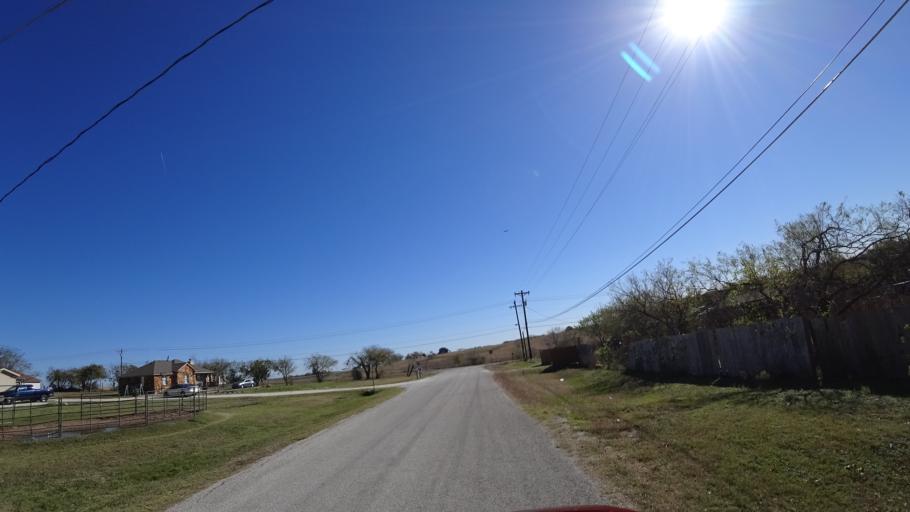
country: US
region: Texas
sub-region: Travis County
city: Garfield
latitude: 30.1035
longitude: -97.5936
